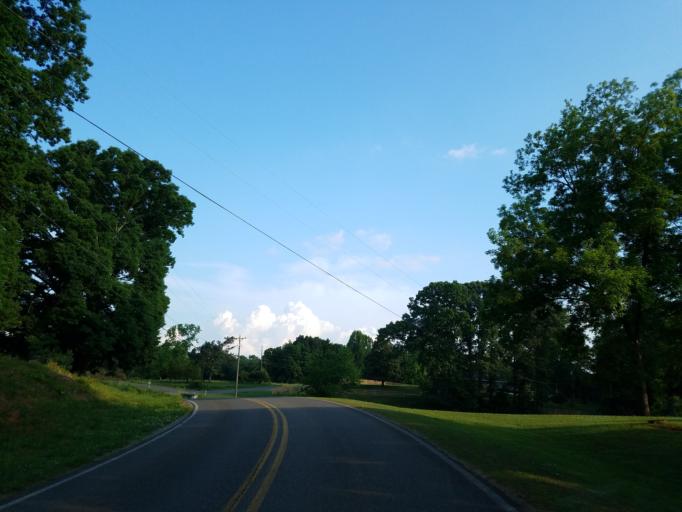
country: US
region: Georgia
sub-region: Cherokee County
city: Ball Ground
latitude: 34.3268
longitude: -84.3682
